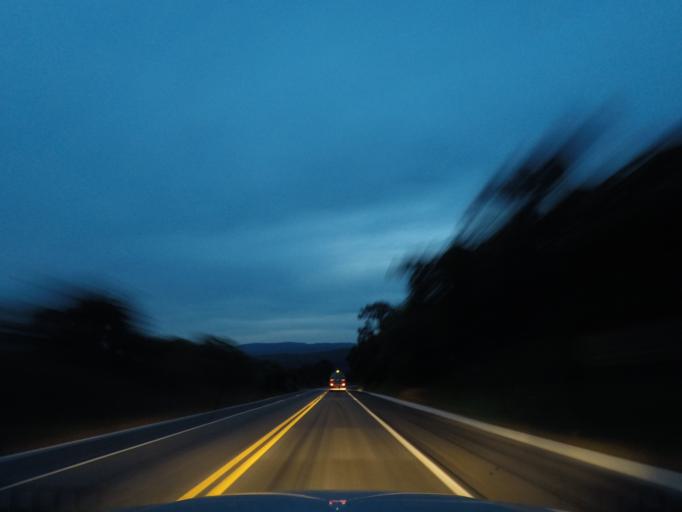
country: BR
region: Bahia
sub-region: Andarai
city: Vera Cruz
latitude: -12.4954
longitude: -41.3205
